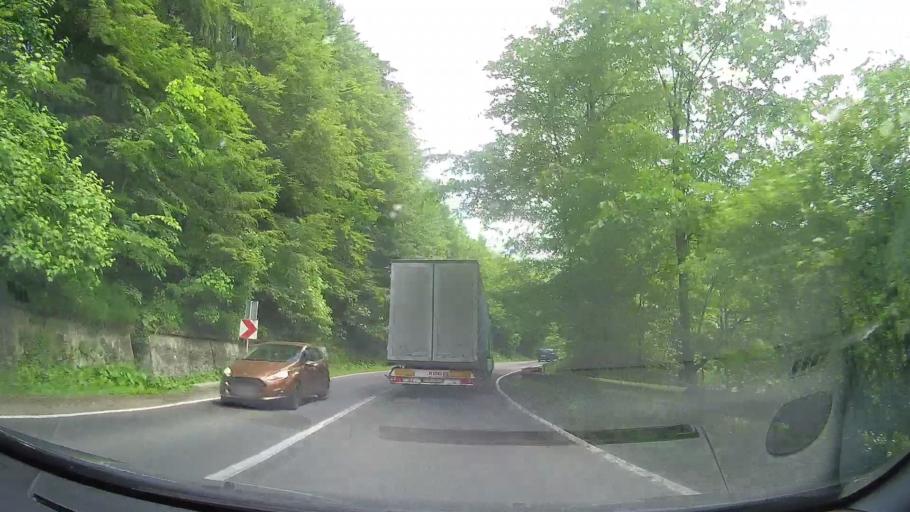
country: RO
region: Prahova
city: Maneciu
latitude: 45.3688
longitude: 25.9294
